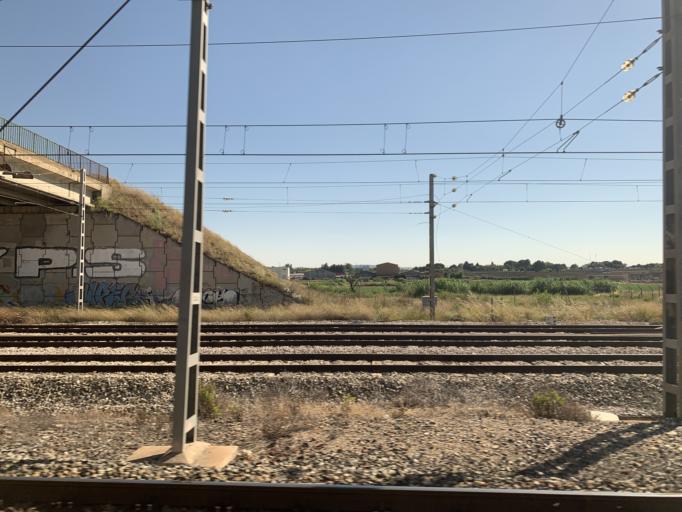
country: ES
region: Aragon
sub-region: Provincia de Zaragoza
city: Oliver-Valdefierro, Oliver, Valdefierro
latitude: 41.6755
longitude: -0.9403
